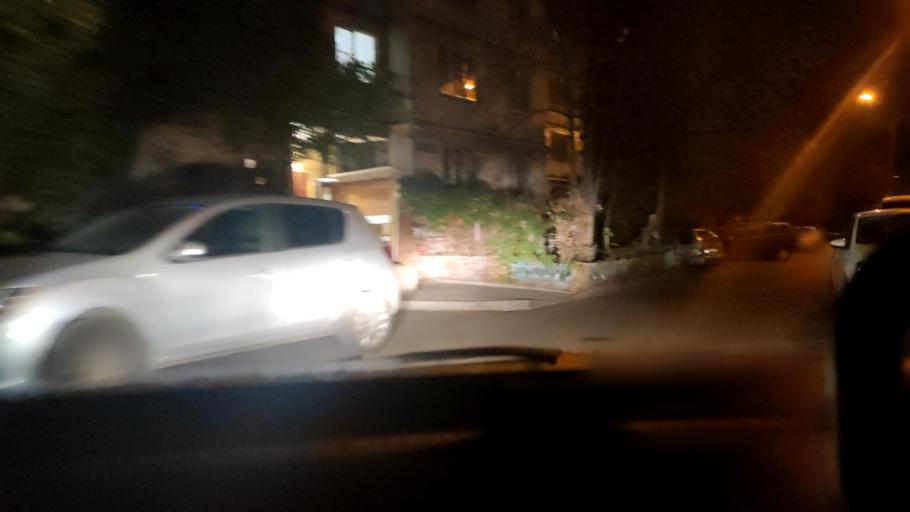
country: RU
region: Voronezj
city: Voronezh
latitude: 51.6390
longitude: 39.2317
